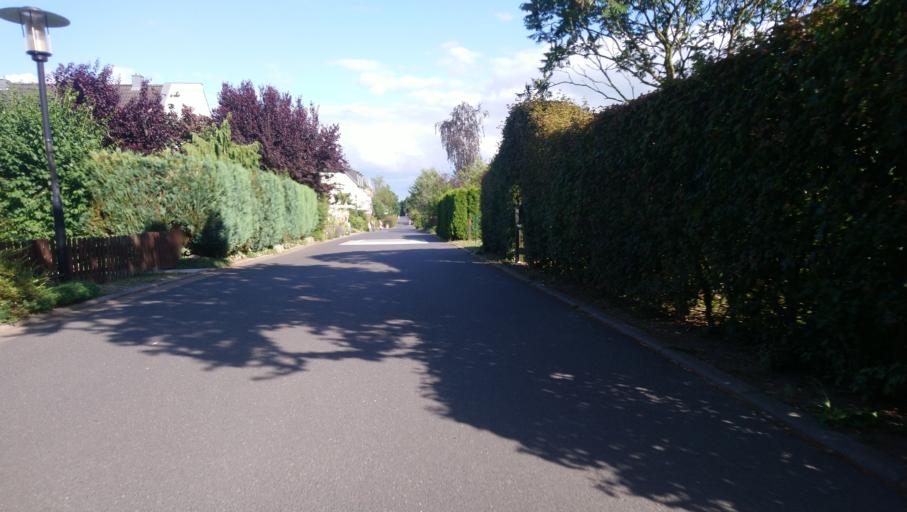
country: DE
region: Mecklenburg-Vorpommern
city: Papendorf
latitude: 54.0593
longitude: 12.1101
